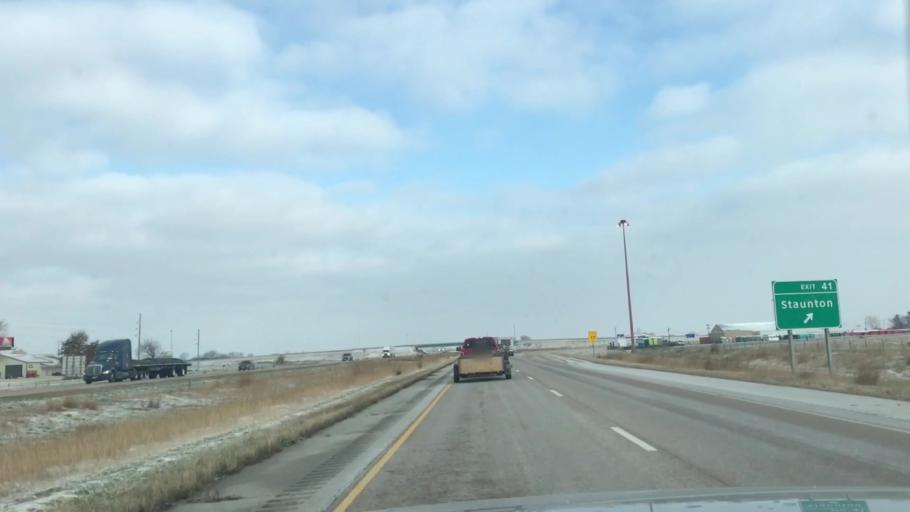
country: US
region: Illinois
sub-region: Macoupin County
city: Staunton
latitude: 39.0151
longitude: -89.7494
